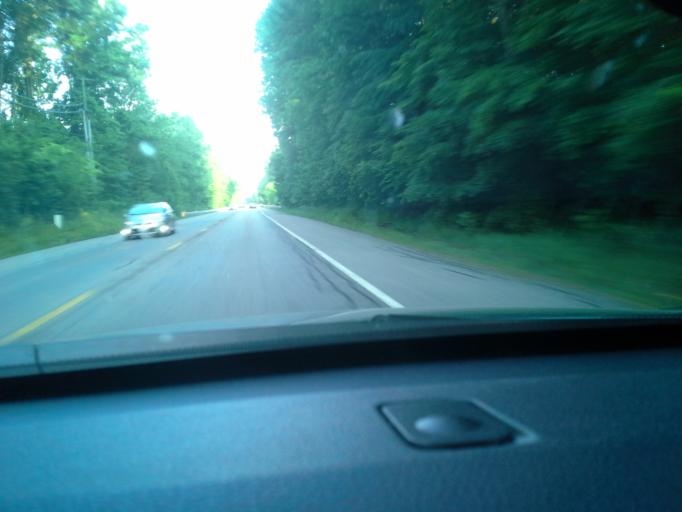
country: US
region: Maryland
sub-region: Calvert County
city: Owings
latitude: 38.7121
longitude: -76.5949
